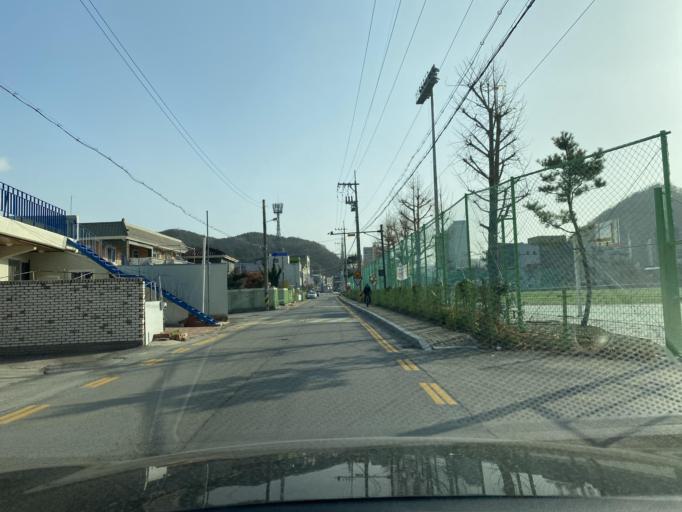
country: KR
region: Chungcheongnam-do
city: Yesan
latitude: 36.6796
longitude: 126.8318
